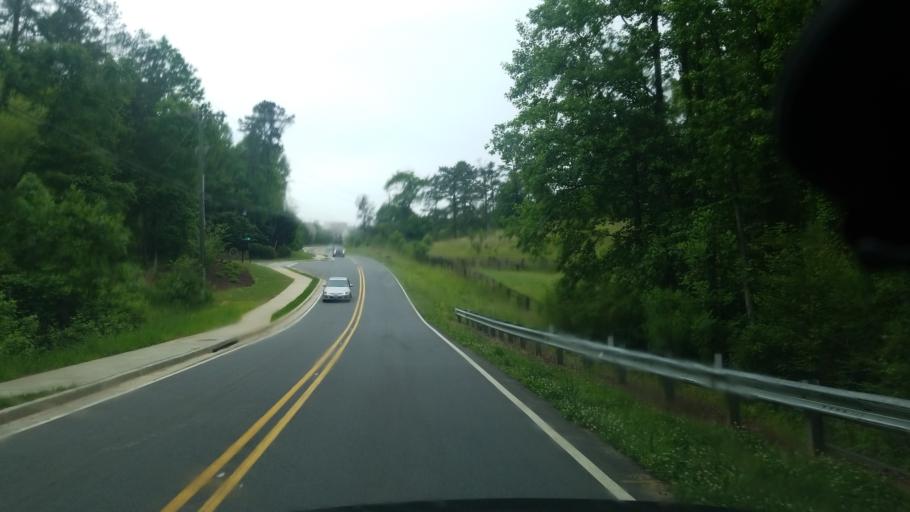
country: US
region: Georgia
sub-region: Gwinnett County
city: Suwanee
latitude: 34.1127
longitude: -84.1264
